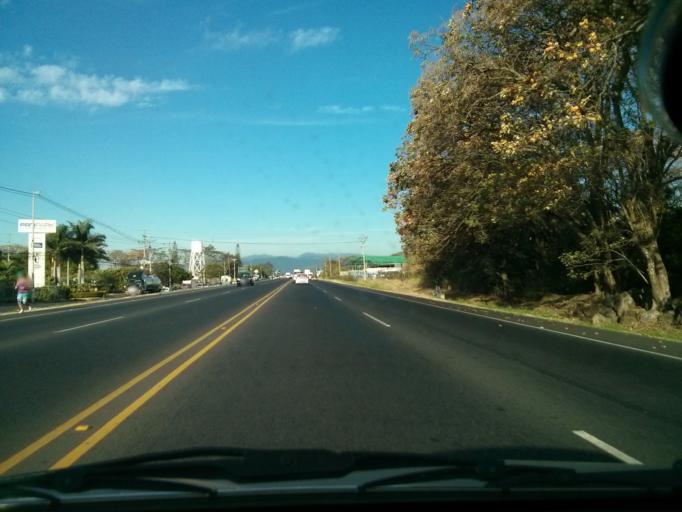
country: CR
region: Alajuela
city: Carrillos
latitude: 9.9955
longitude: -84.2607
